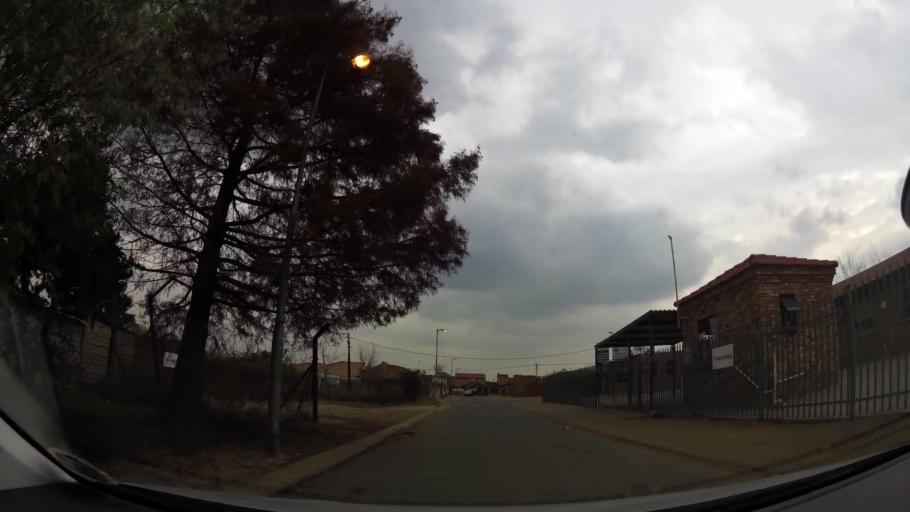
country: ZA
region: Gauteng
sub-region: City of Johannesburg Metropolitan Municipality
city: Soweto
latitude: -26.2617
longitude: 27.8664
